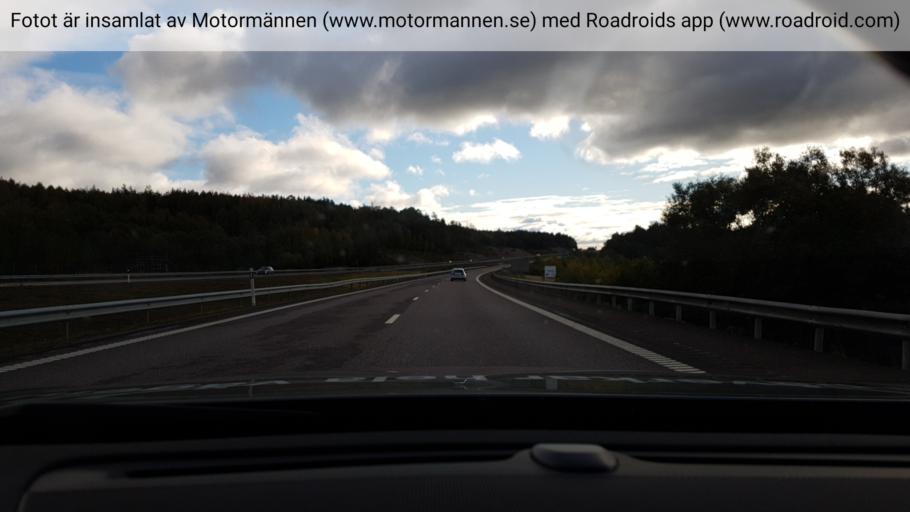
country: SE
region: Soedermanland
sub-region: Nykopings Kommun
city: Stigtomta
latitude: 58.7583
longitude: 16.7071
